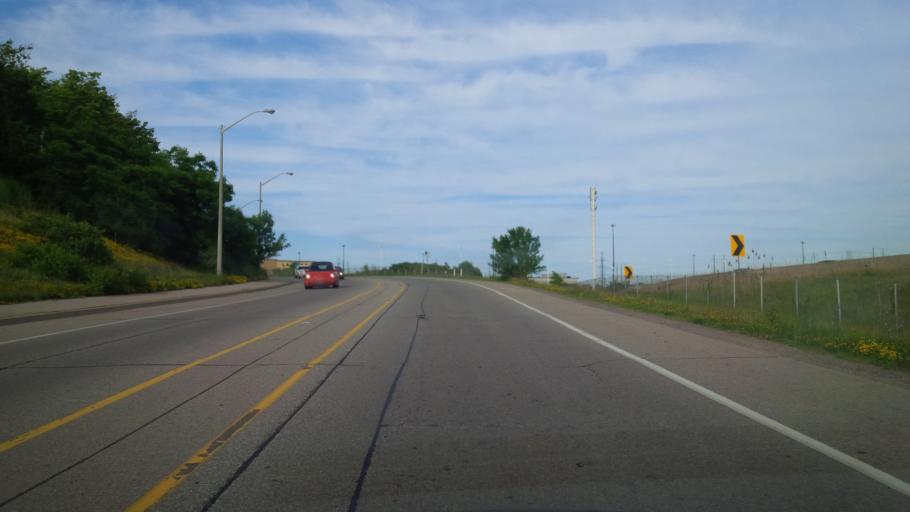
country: CA
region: Ontario
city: Burlington
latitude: 43.3408
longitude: -79.8297
